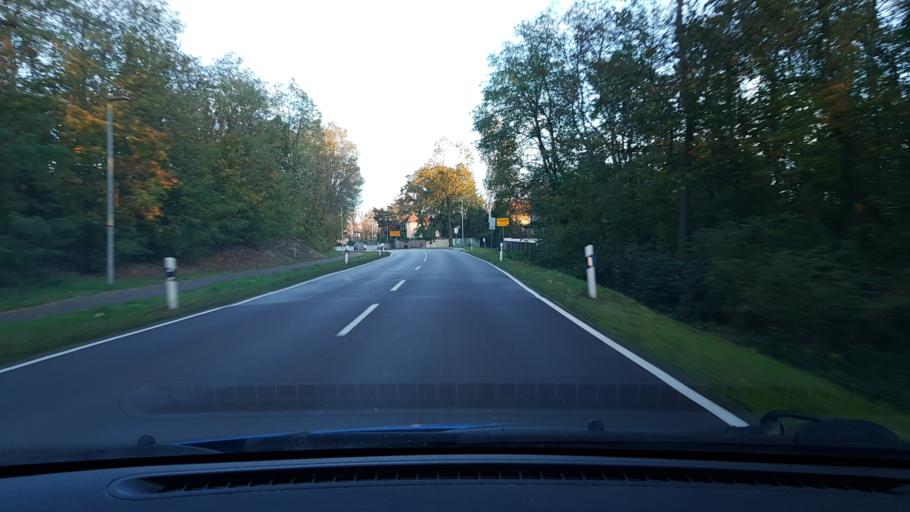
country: DE
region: Saxony-Anhalt
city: Wahlitz
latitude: 52.1341
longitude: 11.7535
